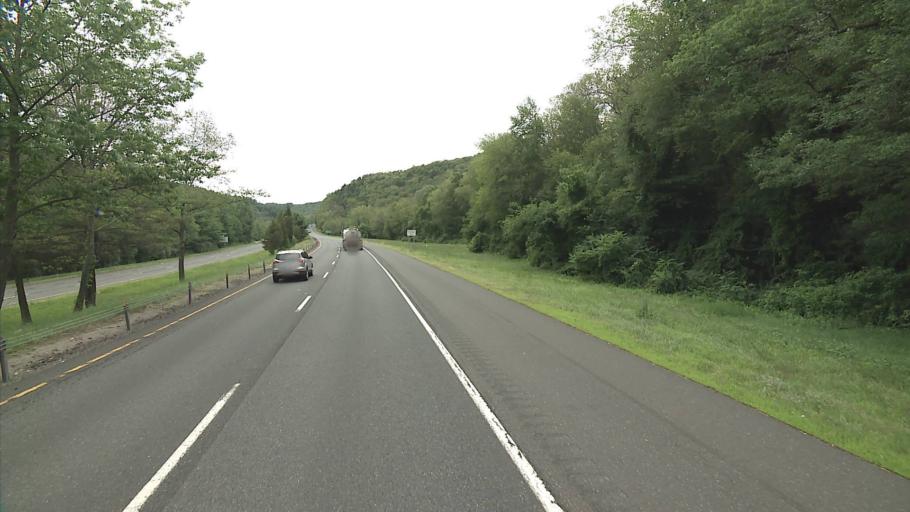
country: US
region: Connecticut
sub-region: Litchfield County
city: Thomaston
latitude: 41.6426
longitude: -73.0822
